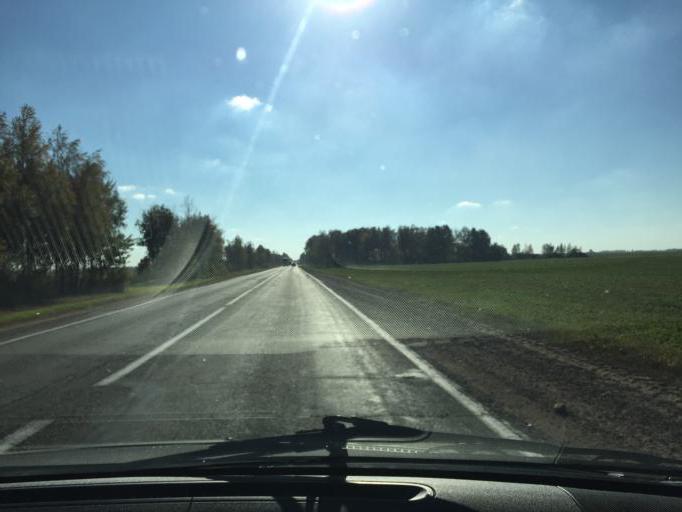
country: BY
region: Minsk
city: Salihorsk
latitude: 52.9117
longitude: 27.4799
